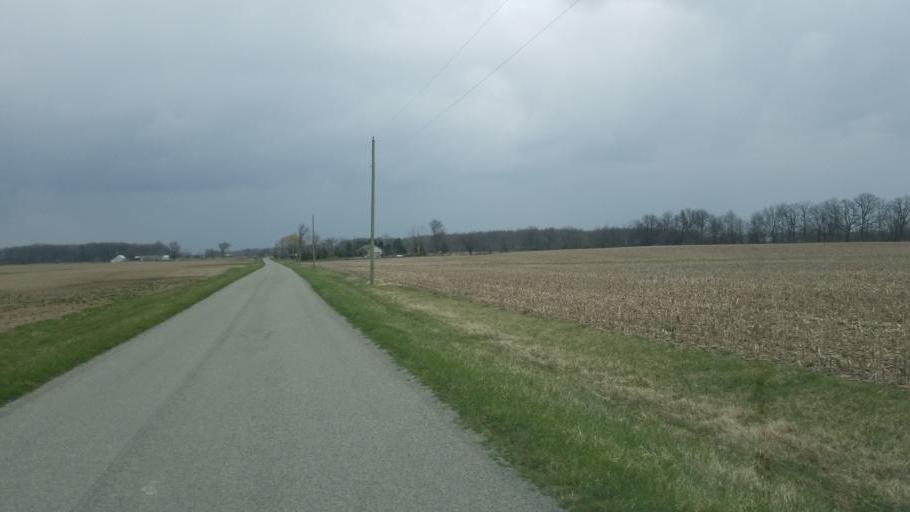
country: US
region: Ohio
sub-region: Union County
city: Richwood
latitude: 40.4188
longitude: -83.3875
